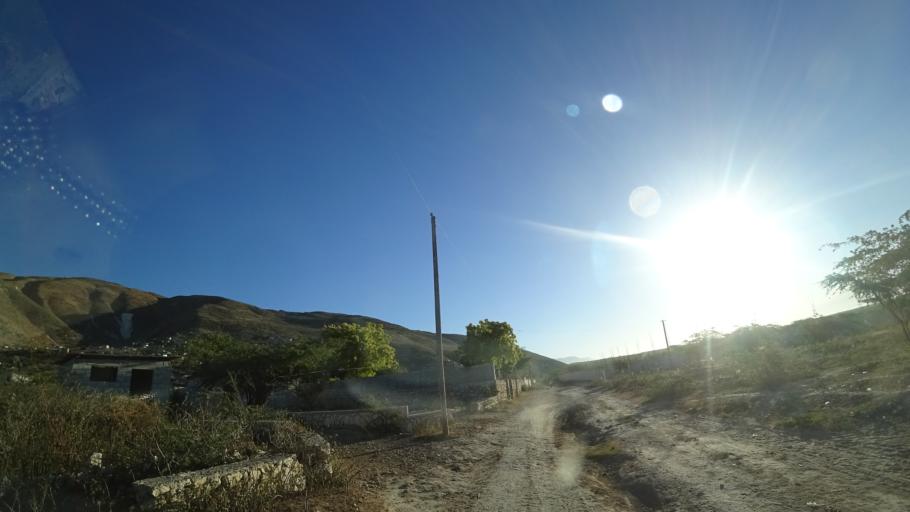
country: HT
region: Ouest
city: Croix des Bouquets
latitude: 18.6627
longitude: -72.2237
